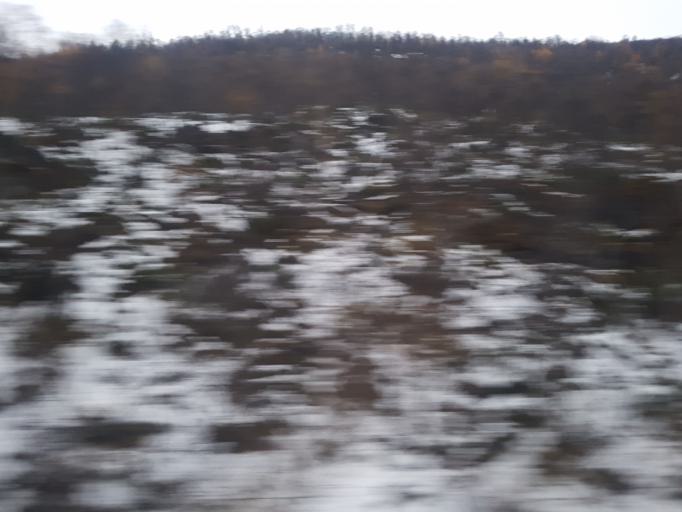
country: NO
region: Sor-Trondelag
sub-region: Oppdal
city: Oppdal
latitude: 62.3314
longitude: 9.6207
